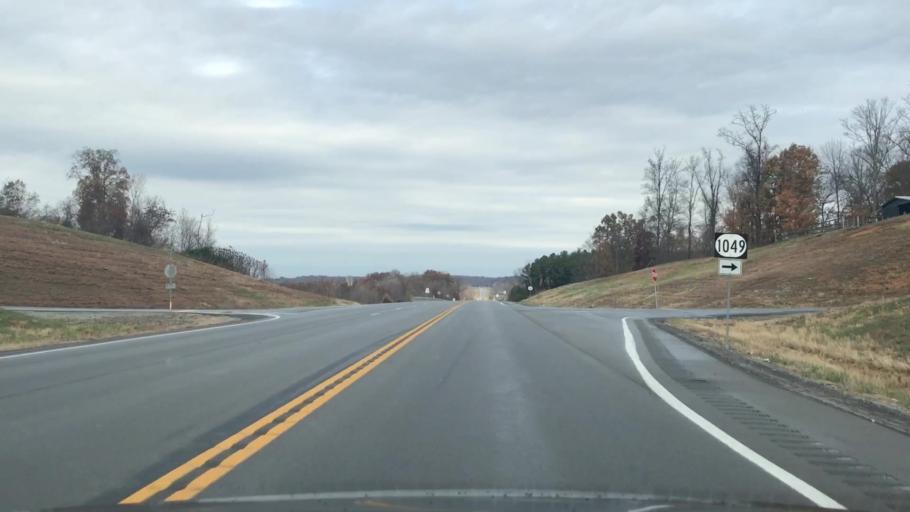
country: US
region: Kentucky
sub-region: Monroe County
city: Tompkinsville
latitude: 36.7905
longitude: -85.6869
